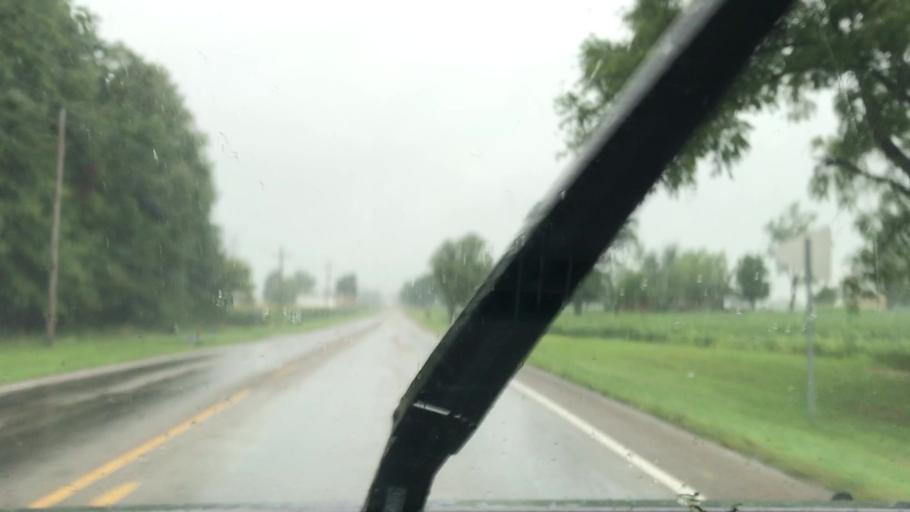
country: US
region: Indiana
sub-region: Hamilton County
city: Sheridan
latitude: 40.1176
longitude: -86.1812
